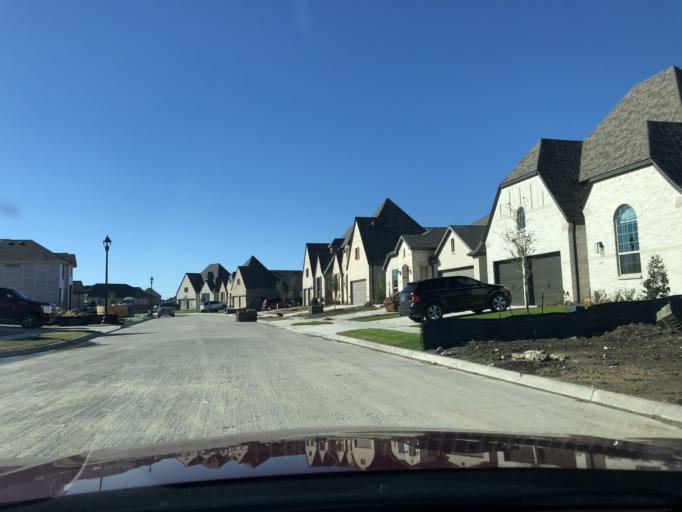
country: US
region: Texas
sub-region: Tarrant County
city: Haslet
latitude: 32.9481
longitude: -97.3924
